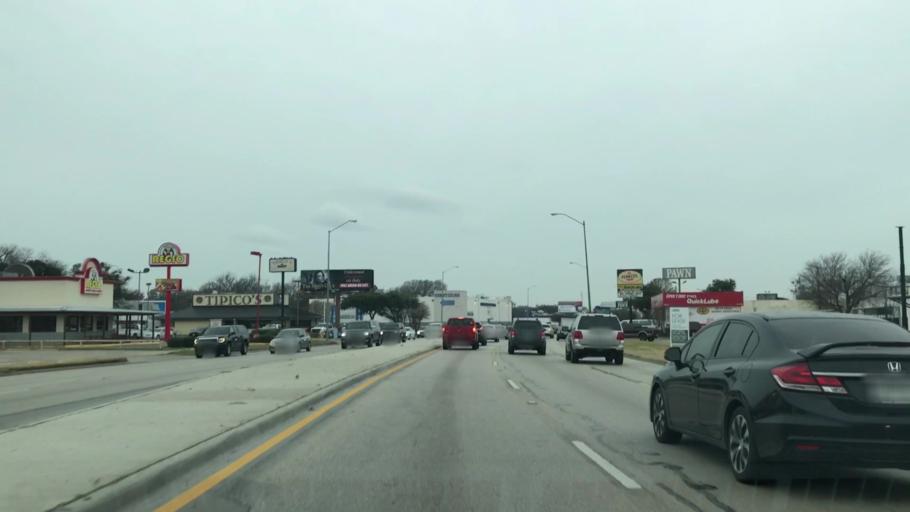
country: US
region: Texas
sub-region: Dallas County
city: University Park
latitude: 32.8554
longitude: -96.8662
